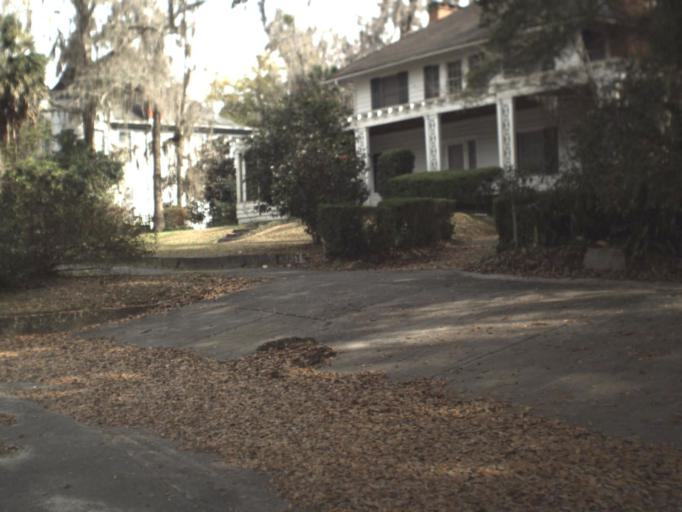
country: US
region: Florida
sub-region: Jefferson County
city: Monticello
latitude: 30.5451
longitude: -83.8761
